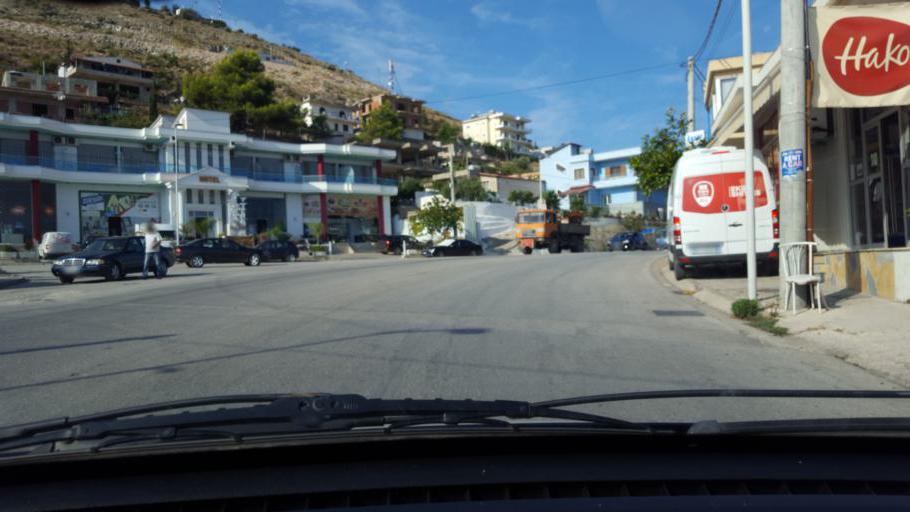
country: AL
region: Vlore
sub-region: Rrethi i Sarandes
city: Sarande
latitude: 39.8692
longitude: 20.0276
